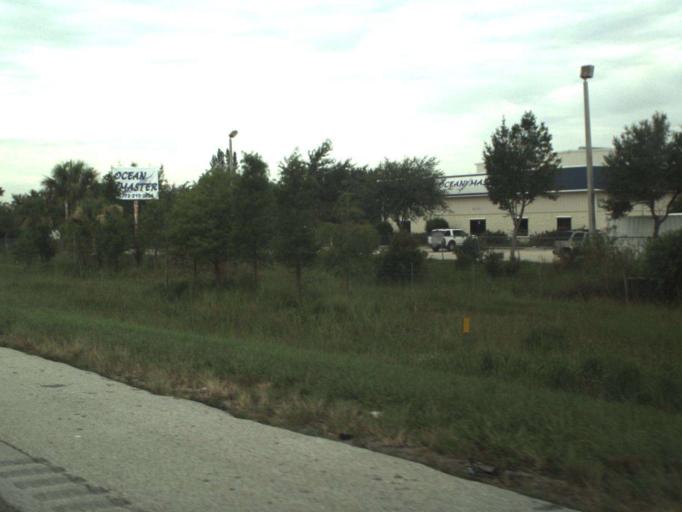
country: US
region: Florida
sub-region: Martin County
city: Palm City
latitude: 27.1001
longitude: -80.2575
